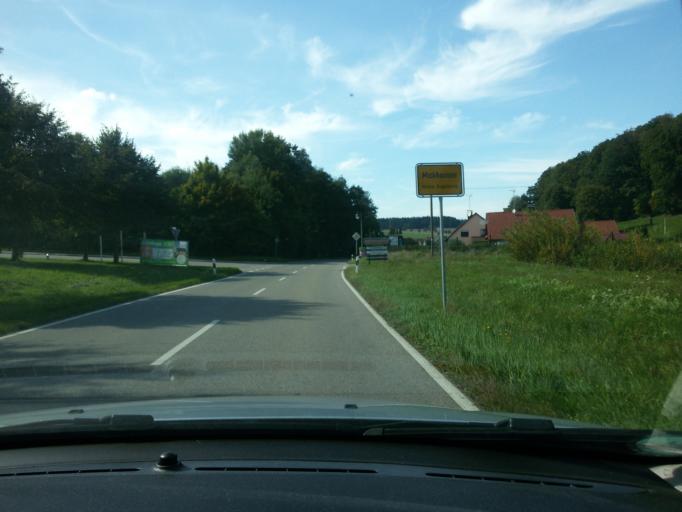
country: DE
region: Bavaria
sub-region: Swabia
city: Mickhausen
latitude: 48.2421
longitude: 10.6449
